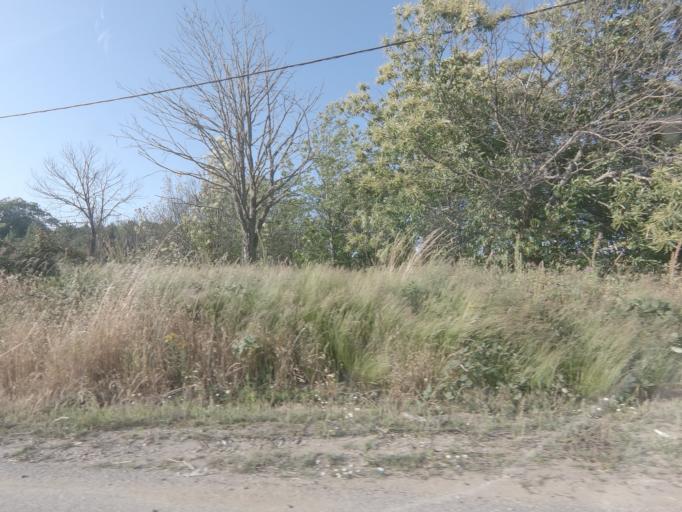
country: PT
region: Vila Real
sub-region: Sabrosa
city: Vilela
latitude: 41.2408
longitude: -7.5994
